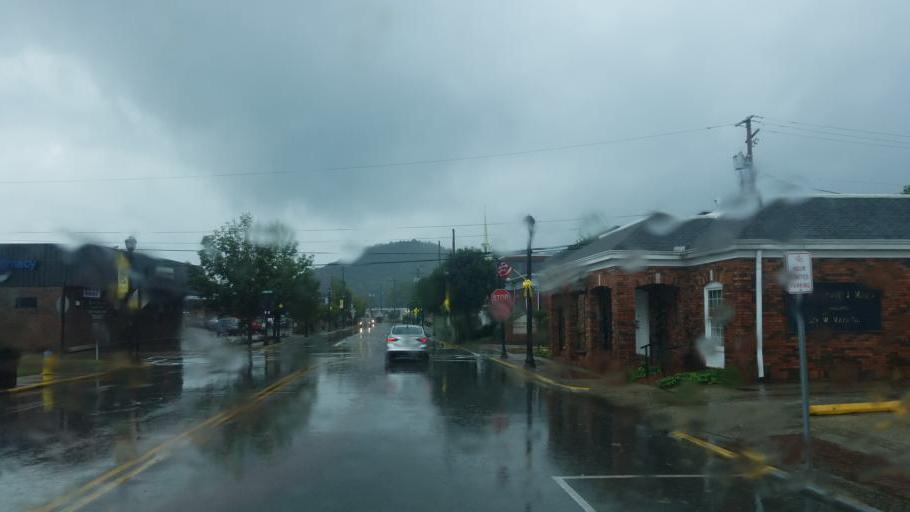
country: US
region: Kentucky
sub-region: Rowan County
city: Morehead
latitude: 38.1808
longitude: -83.4360
